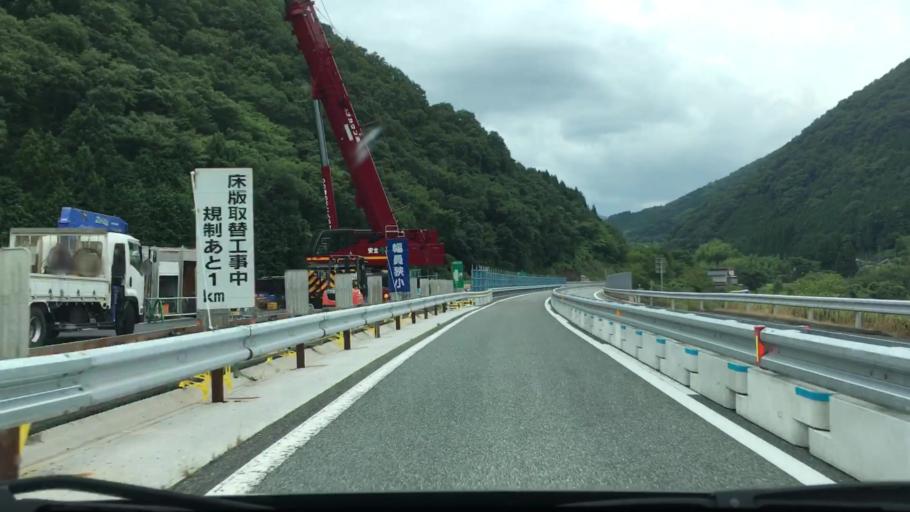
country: JP
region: Okayama
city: Niimi
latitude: 35.0046
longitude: 133.4049
